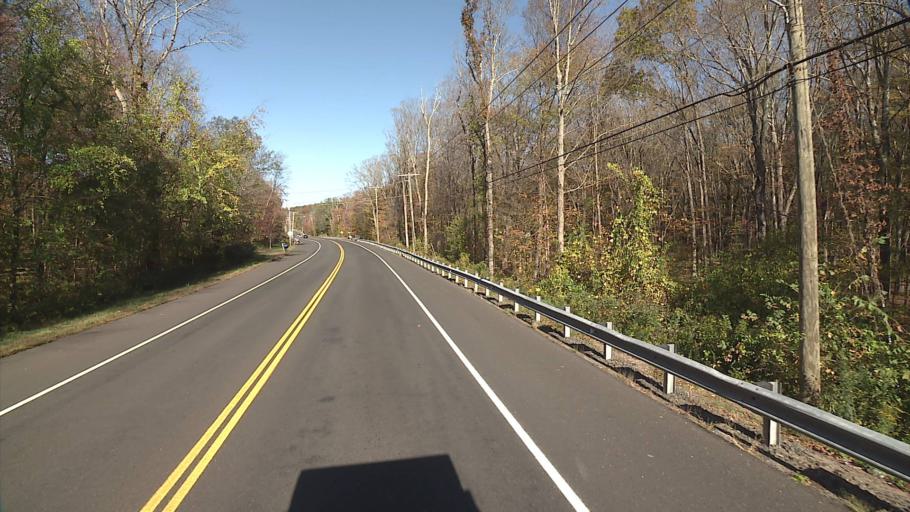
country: US
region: Connecticut
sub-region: Tolland County
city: Coventry Lake
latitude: 41.7774
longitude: -72.4169
